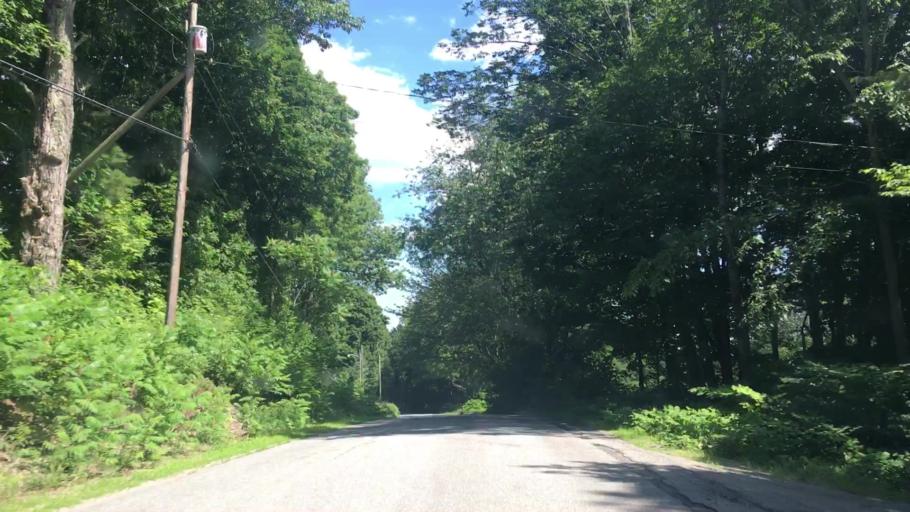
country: US
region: Maine
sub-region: Franklin County
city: Chesterville
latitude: 44.5646
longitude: -70.1419
